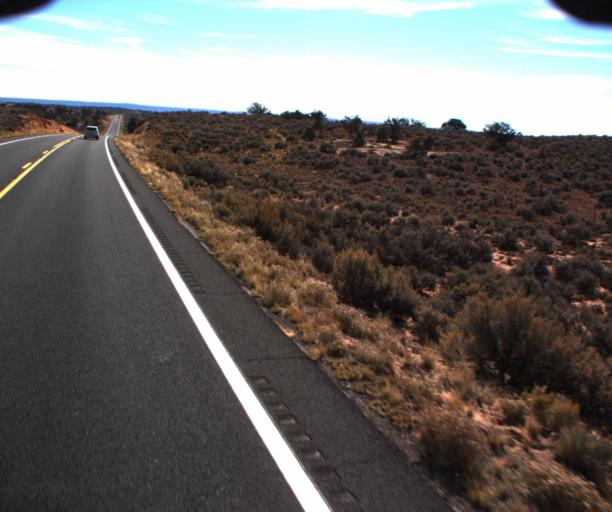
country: US
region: Arizona
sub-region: Coconino County
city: Kaibito
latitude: 36.5608
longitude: -110.7217
